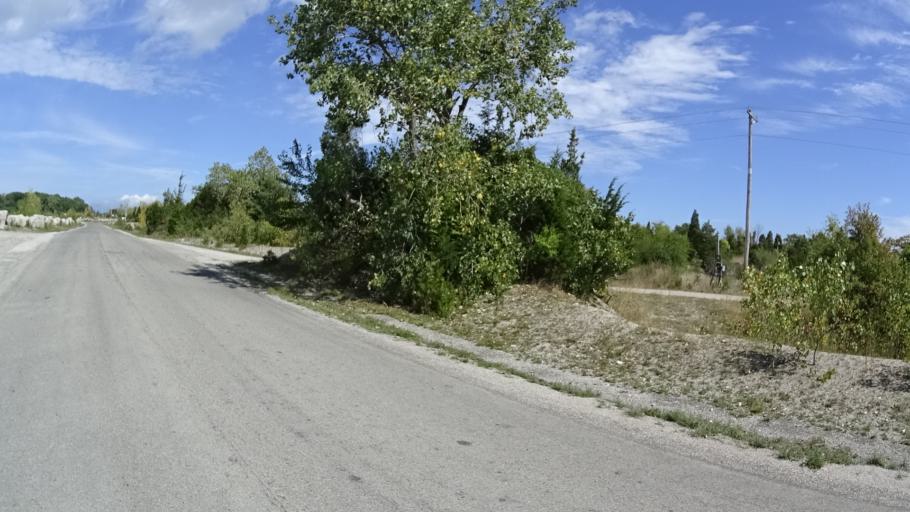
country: US
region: Ohio
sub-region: Erie County
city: Sandusky
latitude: 41.6015
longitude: -82.7211
